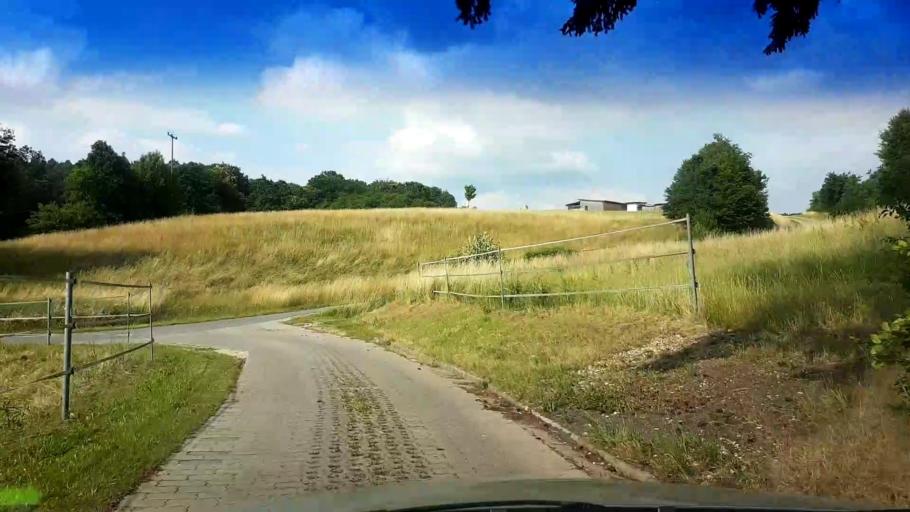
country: DE
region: Bavaria
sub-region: Upper Franconia
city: Walsdorf
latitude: 49.8759
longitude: 10.7995
